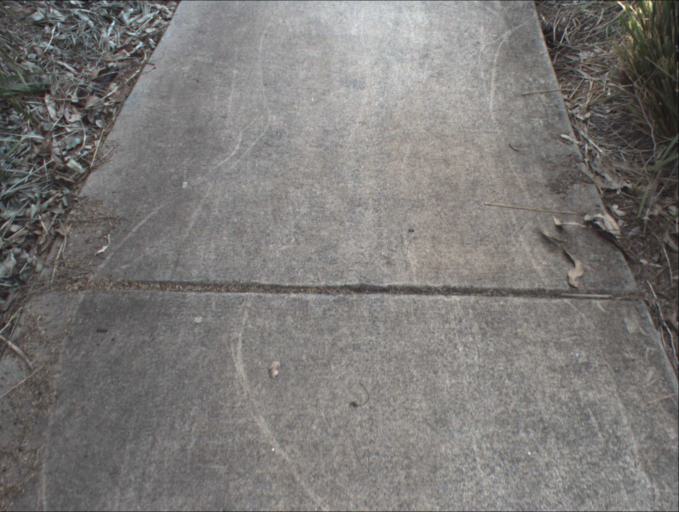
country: AU
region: Queensland
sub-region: Logan
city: North Maclean
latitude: -27.8029
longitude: 152.9558
